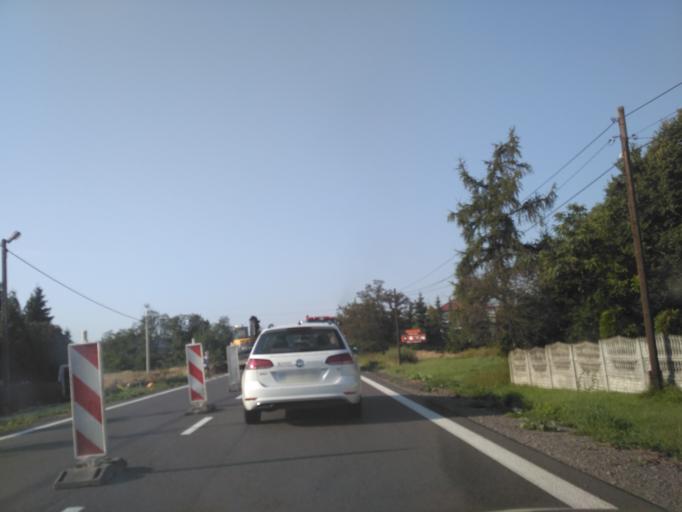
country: PL
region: Subcarpathian Voivodeship
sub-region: Powiat nizanski
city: Nisko
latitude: 50.5027
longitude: 22.1401
